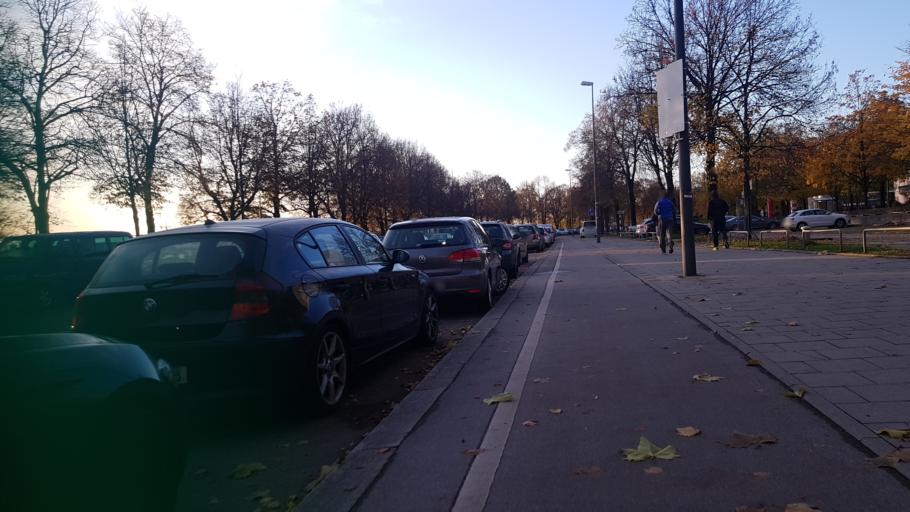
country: DE
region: Bavaria
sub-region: Upper Bavaria
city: Munich
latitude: 48.1342
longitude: 11.5469
